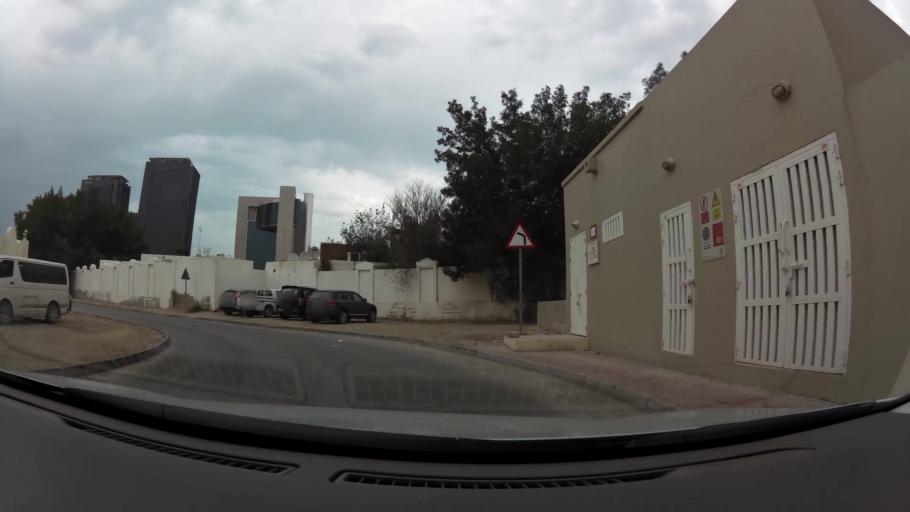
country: QA
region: Baladiyat ad Dawhah
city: Doha
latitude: 25.2790
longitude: 51.5045
